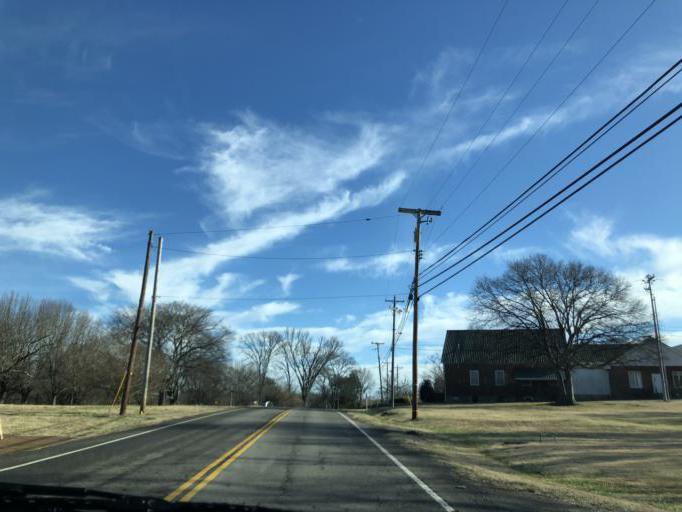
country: US
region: Tennessee
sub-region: Wilson County
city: Green Hill
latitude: 36.1736
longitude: -86.5767
